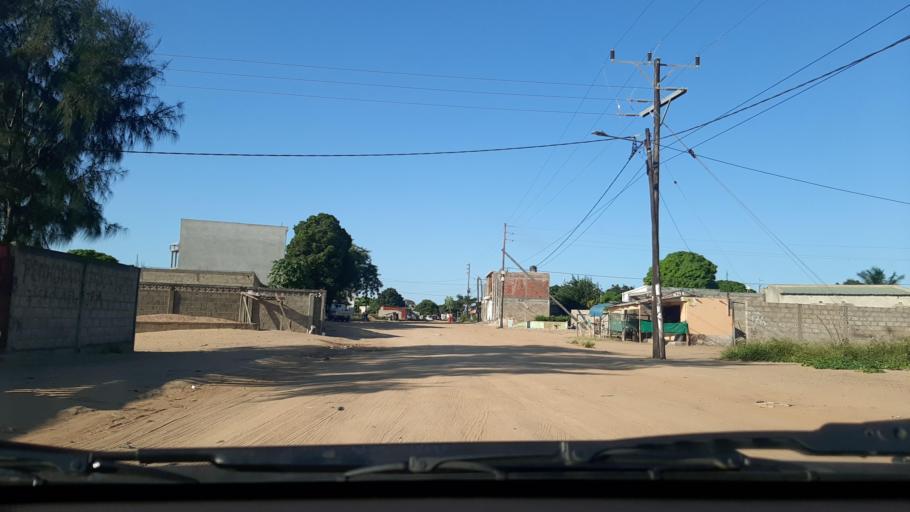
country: MZ
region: Maputo City
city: Maputo
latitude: -25.8020
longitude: 32.5480
